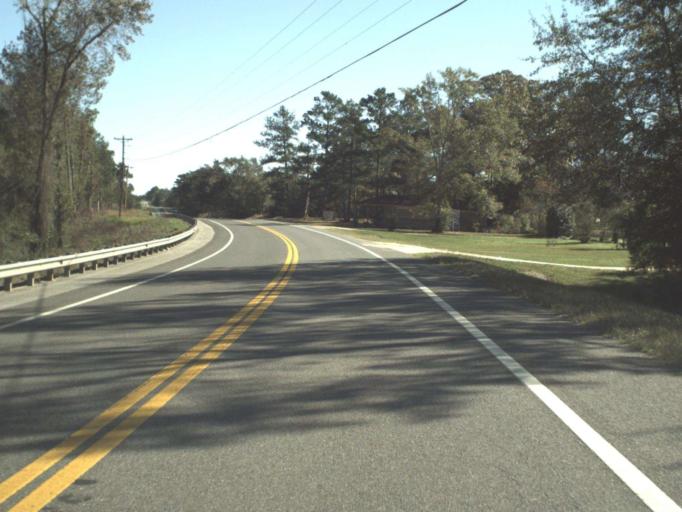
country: US
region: Florida
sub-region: Escambia County
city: Century
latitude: 30.9492
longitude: -87.1964
